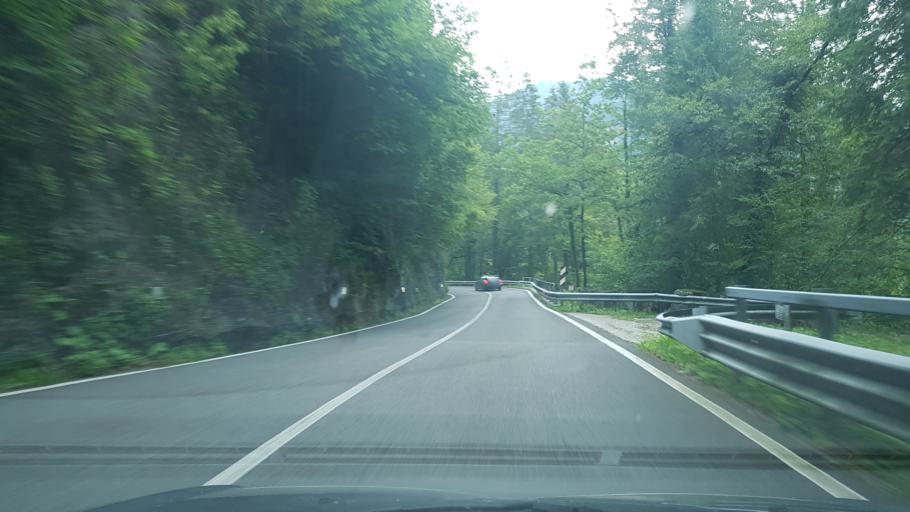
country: IT
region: Friuli Venezia Giulia
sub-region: Provincia di Udine
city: Comeglians
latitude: 46.5256
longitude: 12.8693
